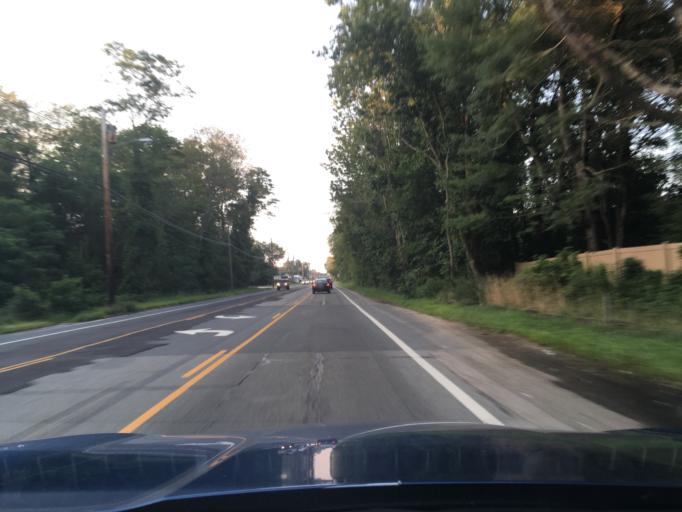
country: US
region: Rhode Island
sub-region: Washington County
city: North Kingstown
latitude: 41.5825
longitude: -71.4595
